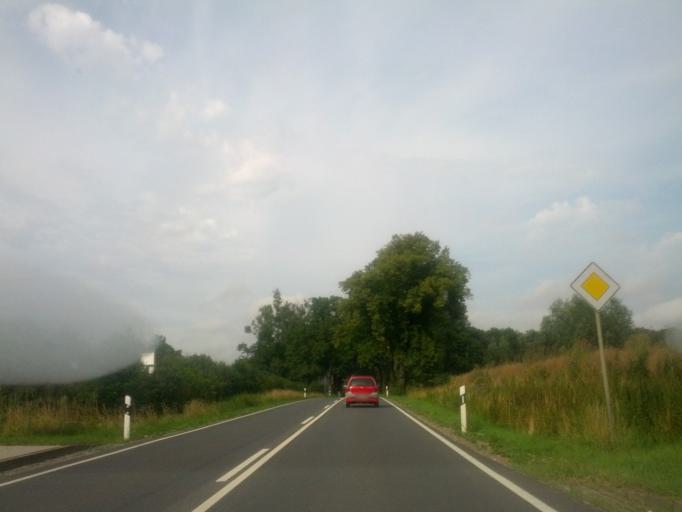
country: DE
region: Mecklenburg-Vorpommern
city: Sellin
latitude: 53.9363
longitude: 11.6074
